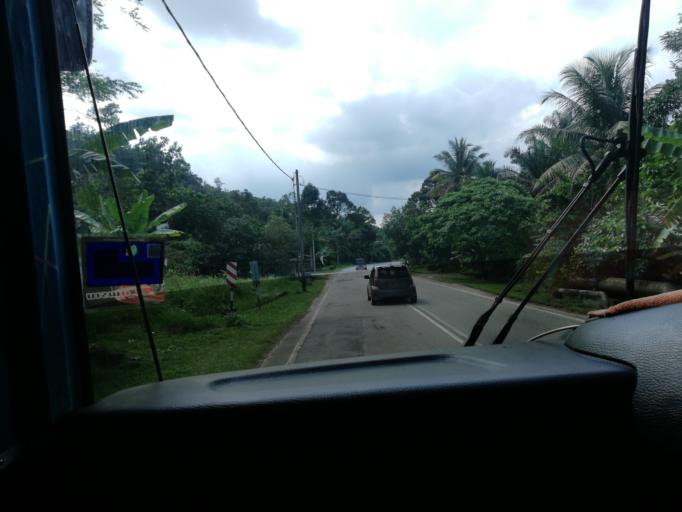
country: MY
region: Kedah
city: Kulim
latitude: 5.2965
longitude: 100.6243
